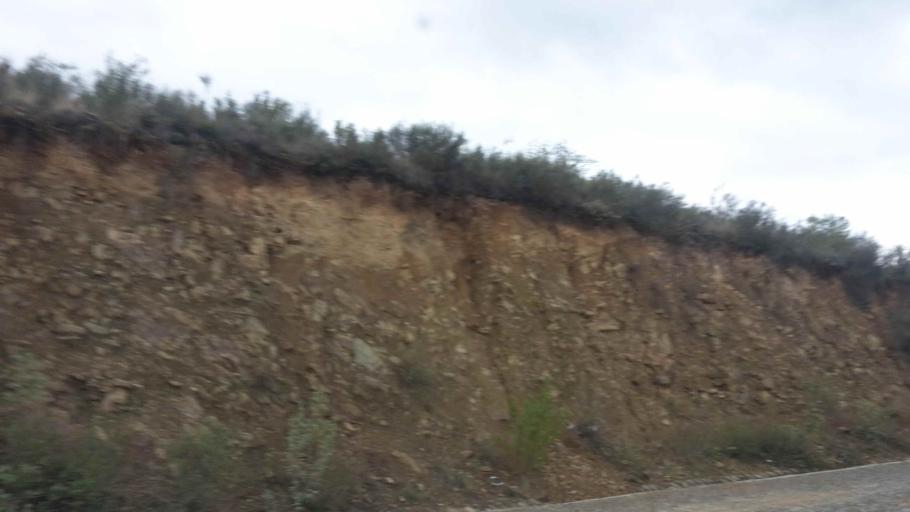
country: BO
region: Cochabamba
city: Cochabamba
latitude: -17.3701
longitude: -66.0637
